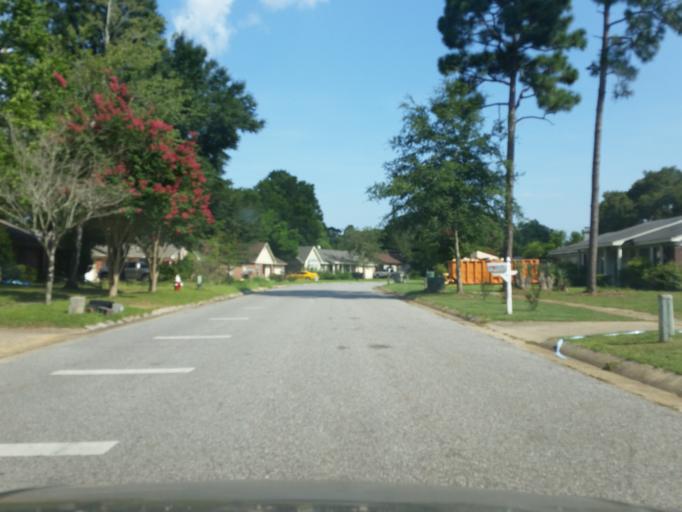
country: US
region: Florida
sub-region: Escambia County
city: Ferry Pass
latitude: 30.5122
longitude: -87.1816
